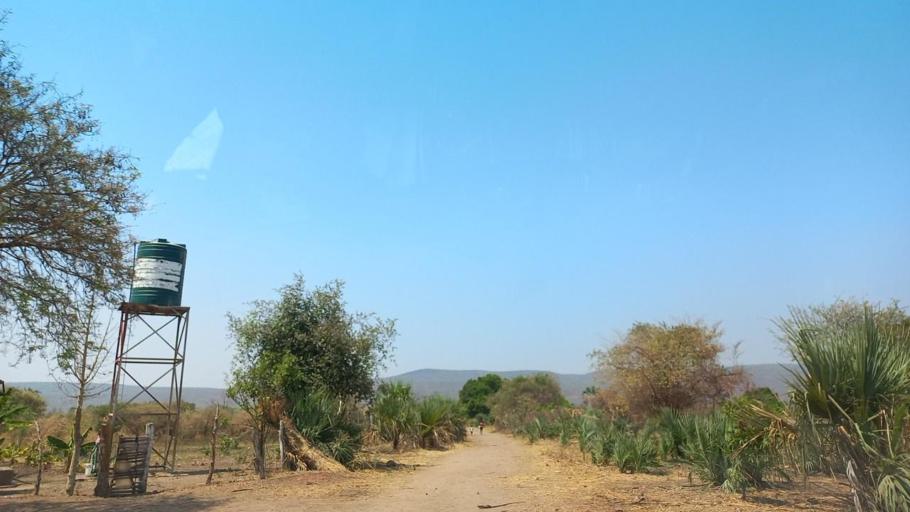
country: ZM
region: Lusaka
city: Luangwa
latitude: -15.1963
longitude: 30.1916
